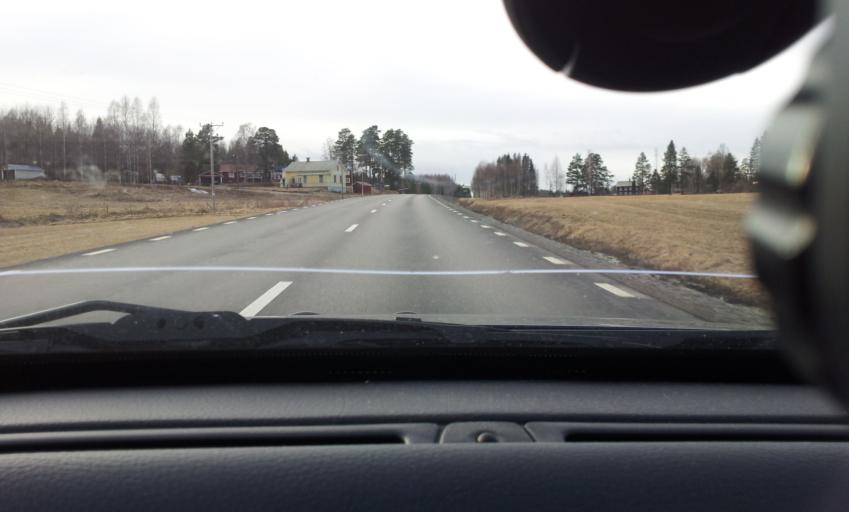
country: SE
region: Gaevleborg
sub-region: Ljusdals Kommun
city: Farila
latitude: 61.8650
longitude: 15.7356
